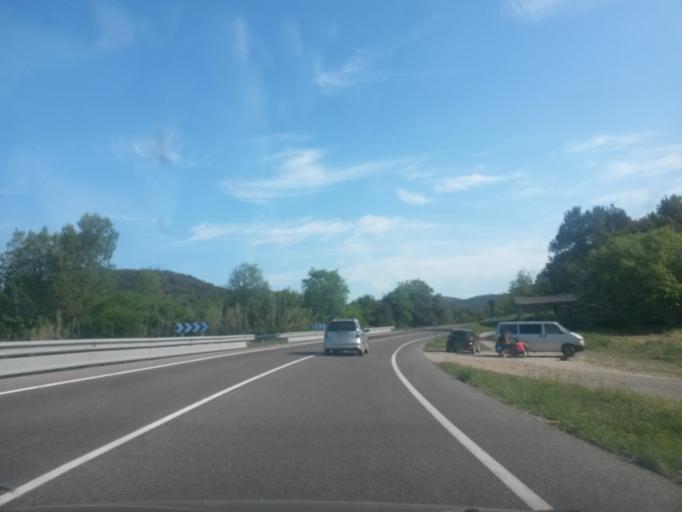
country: ES
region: Catalonia
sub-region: Provincia de Girona
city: Sant Feliu de Pallerols
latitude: 42.0928
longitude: 2.4931
